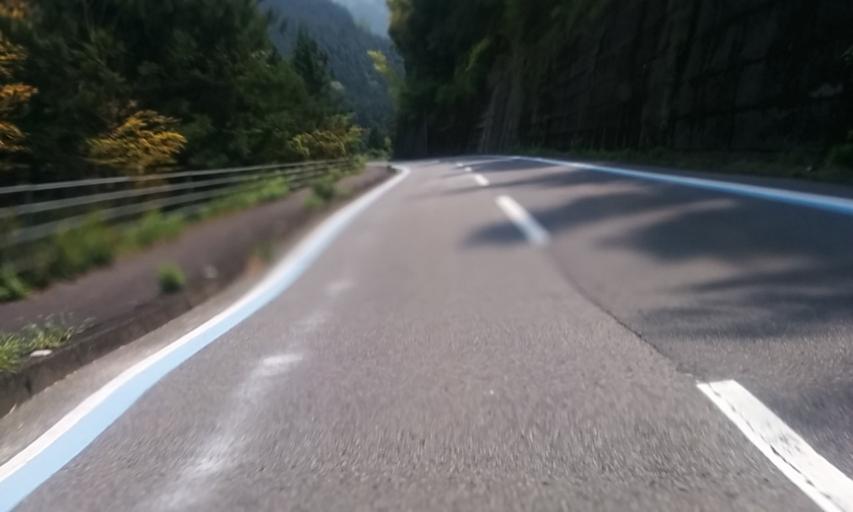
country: JP
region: Ehime
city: Saijo
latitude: 33.8521
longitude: 133.2002
